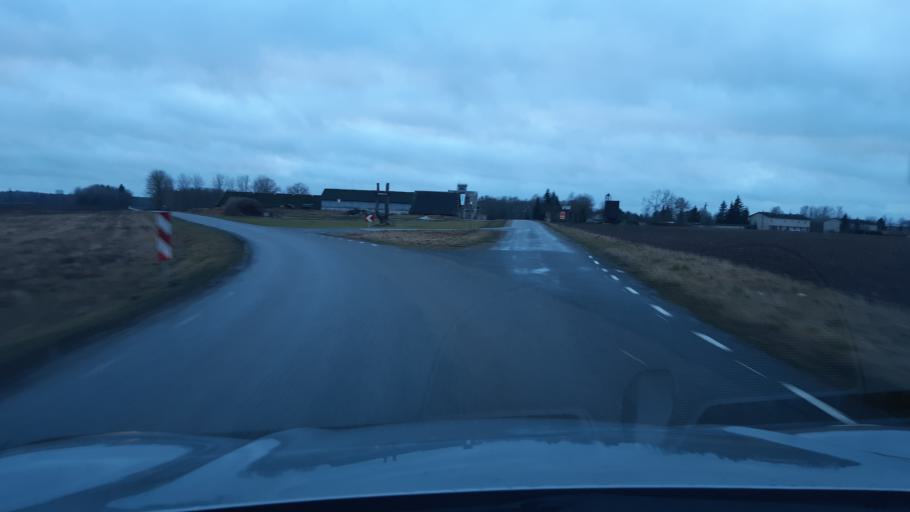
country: EE
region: Raplamaa
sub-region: Rapla vald
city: Rapla
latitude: 59.0453
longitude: 24.6767
